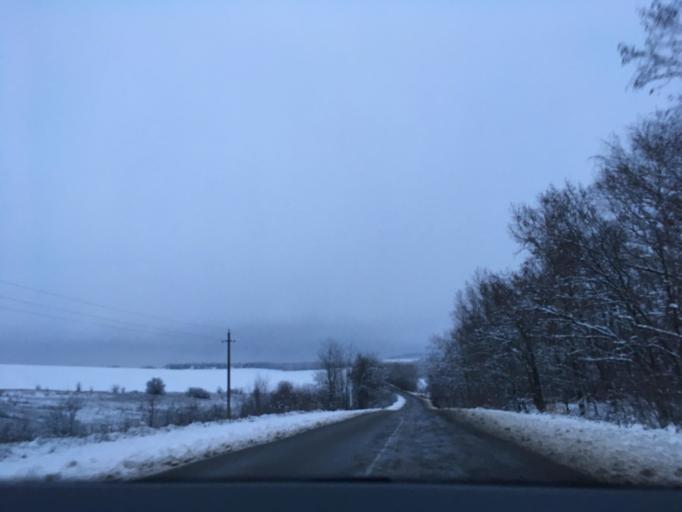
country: RU
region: Voronezj
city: Verkhniy Mamon
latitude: 50.0522
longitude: 40.2479
